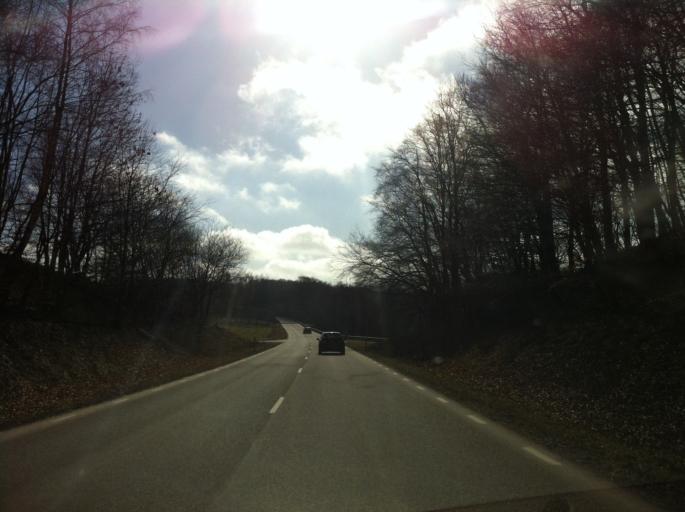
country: SE
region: Skane
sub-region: Bastads Kommun
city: Forslov
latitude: 56.3928
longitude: 12.8070
